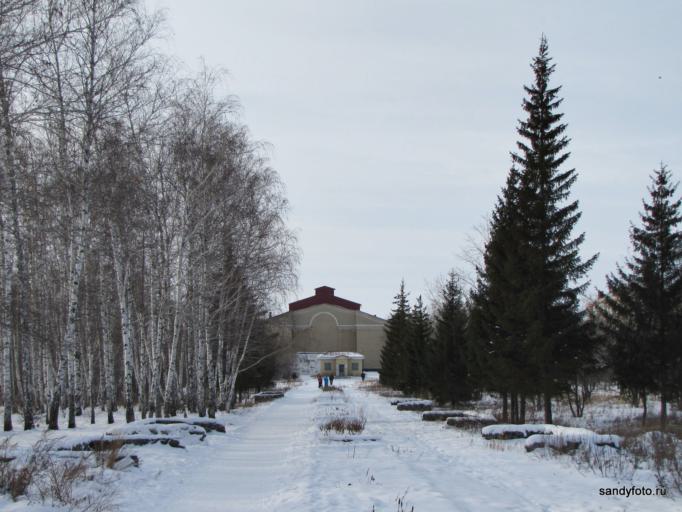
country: RU
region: Chelyabinsk
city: Troitsk
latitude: 54.0482
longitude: 61.6357
